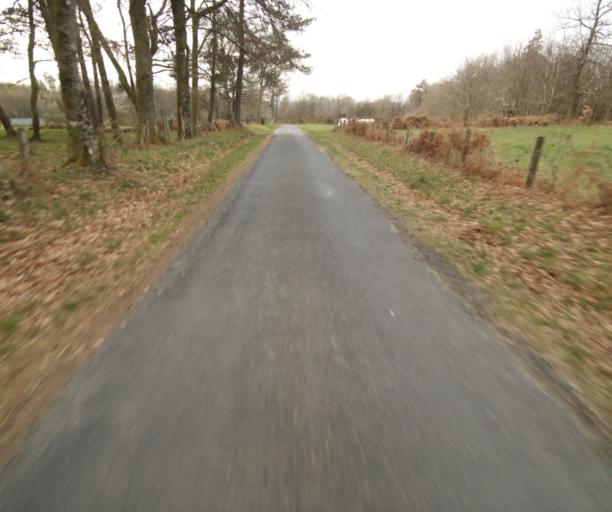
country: FR
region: Limousin
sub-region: Departement de la Correze
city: Correze
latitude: 45.4430
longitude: 1.8212
